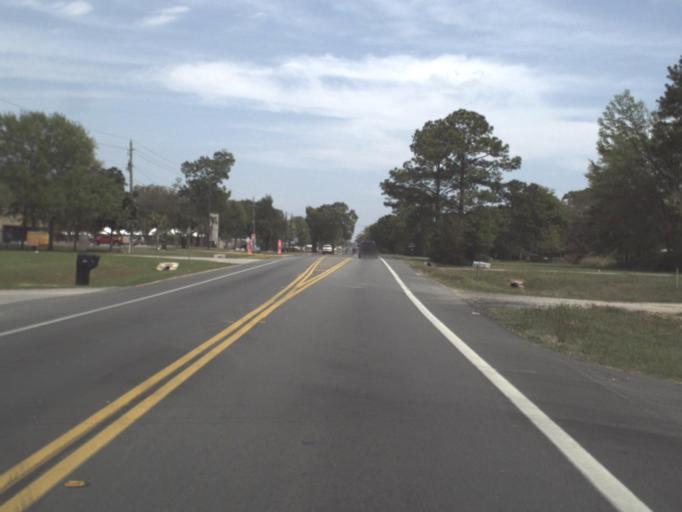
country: US
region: Florida
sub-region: Escambia County
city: Ensley
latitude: 30.5344
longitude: -87.3237
